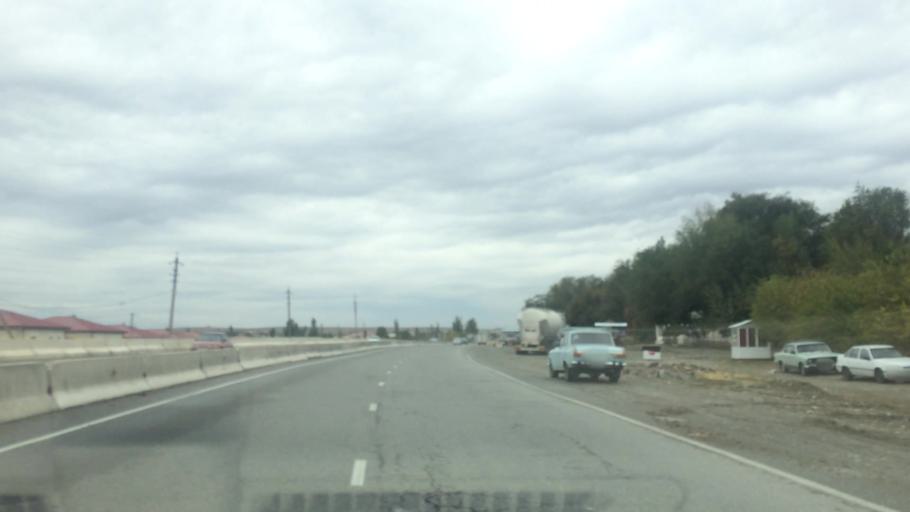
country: UZ
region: Jizzax
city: Jizzax
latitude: 39.9740
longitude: 67.5604
